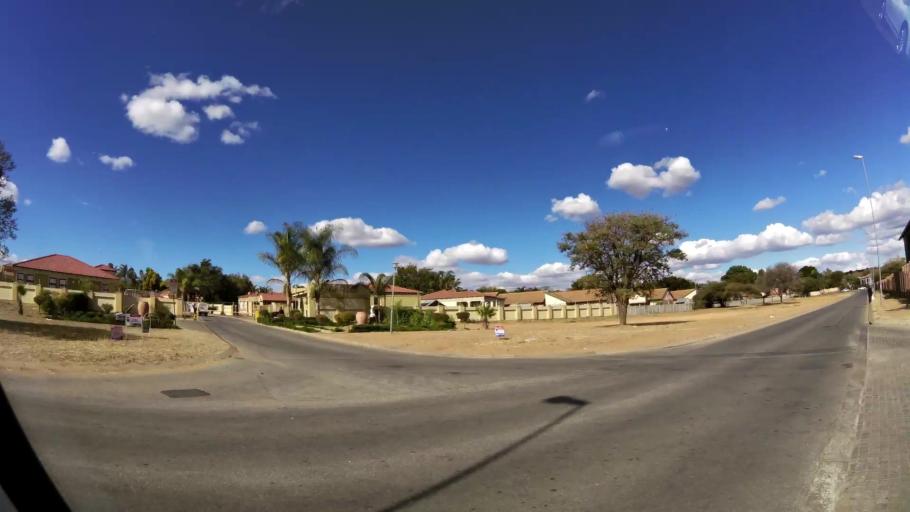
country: ZA
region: Limpopo
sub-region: Capricorn District Municipality
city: Polokwane
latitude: -23.8890
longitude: 29.4754
